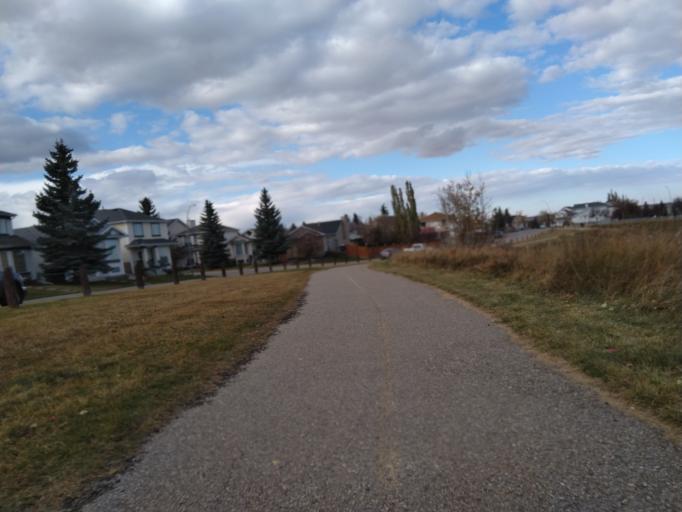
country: CA
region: Alberta
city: Calgary
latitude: 51.1453
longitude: -114.1154
